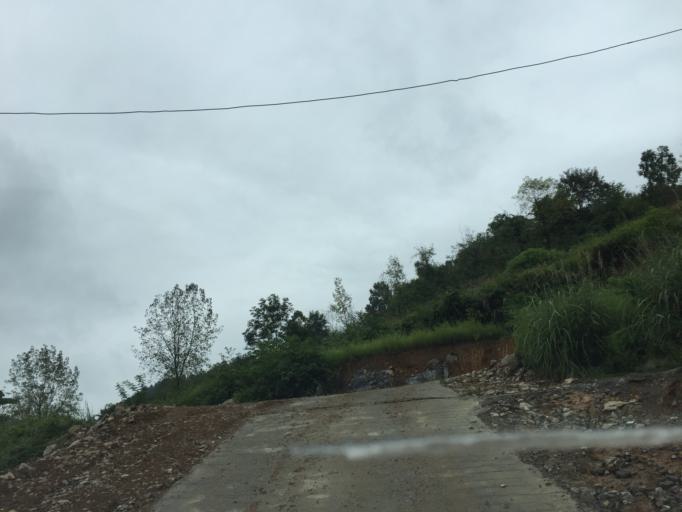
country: CN
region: Guizhou Sheng
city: Yantang
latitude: 28.2075
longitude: 108.0866
